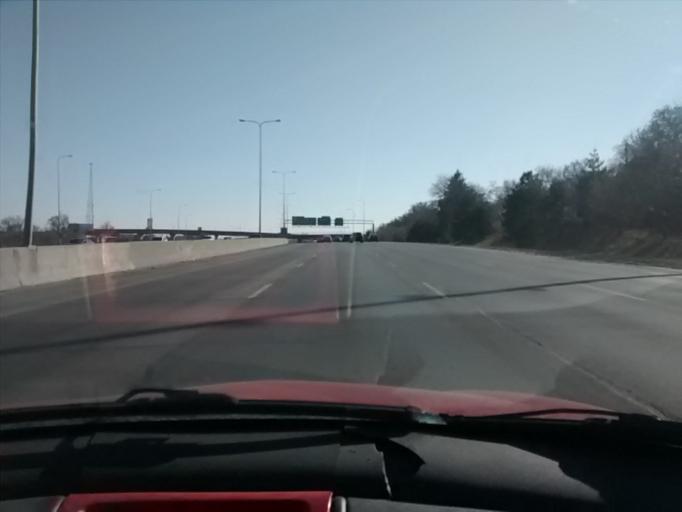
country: US
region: Nebraska
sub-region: Douglas County
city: Omaha
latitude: 41.2341
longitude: -95.9546
